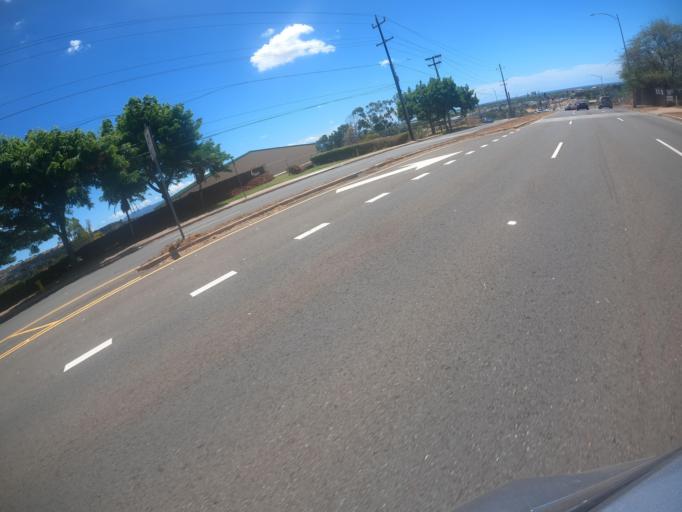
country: US
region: Hawaii
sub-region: Honolulu County
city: Makakilo City
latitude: 21.3433
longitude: -158.0789
